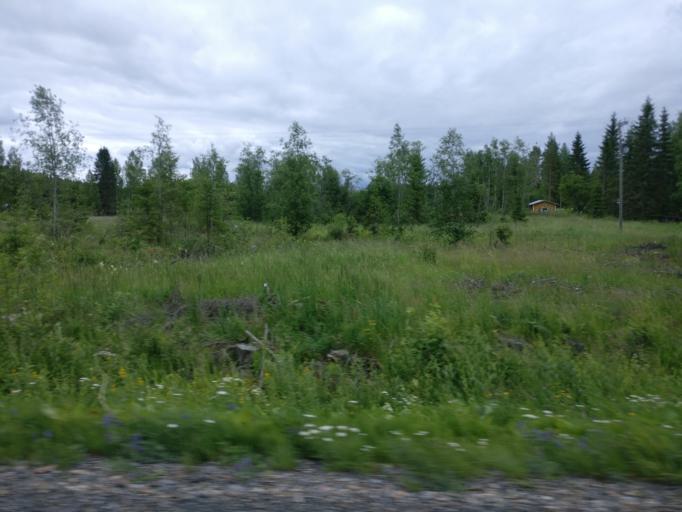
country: FI
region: Northern Savo
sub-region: Varkaus
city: Leppaevirta
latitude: 62.6014
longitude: 27.6134
